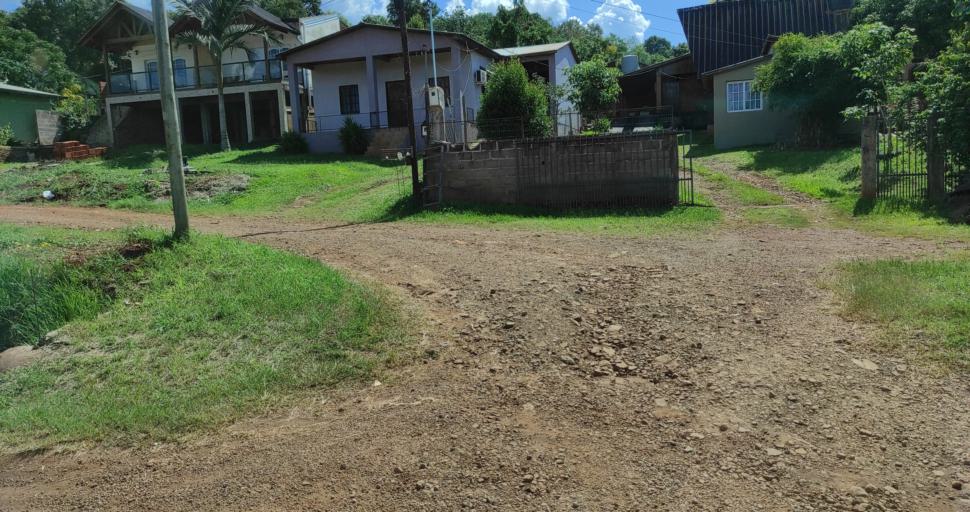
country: AR
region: Misiones
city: El Soberbio
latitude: -27.2864
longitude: -54.1988
